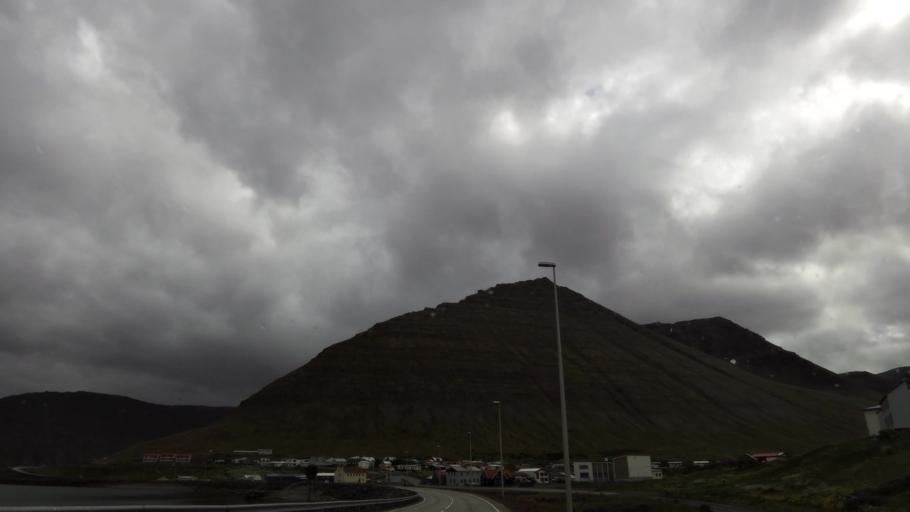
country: IS
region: Westfjords
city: Isafjoerdur
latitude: 66.1138
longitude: -23.1211
